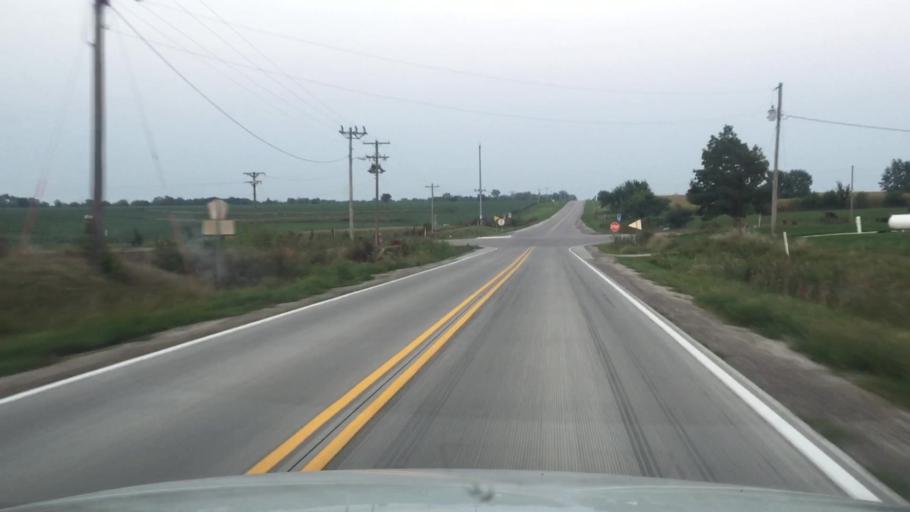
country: US
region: Iowa
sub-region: Warren County
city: Indianola
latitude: 41.1829
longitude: -93.5015
